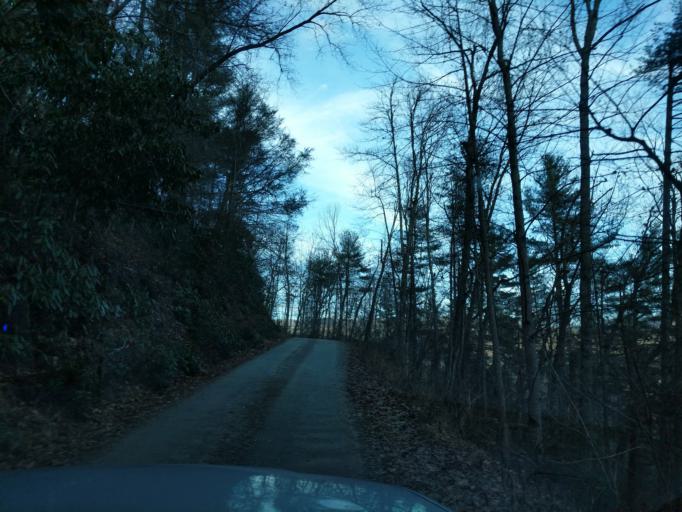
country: US
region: North Carolina
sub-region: Haywood County
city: Cove Creek
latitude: 35.7433
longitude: -83.0430
